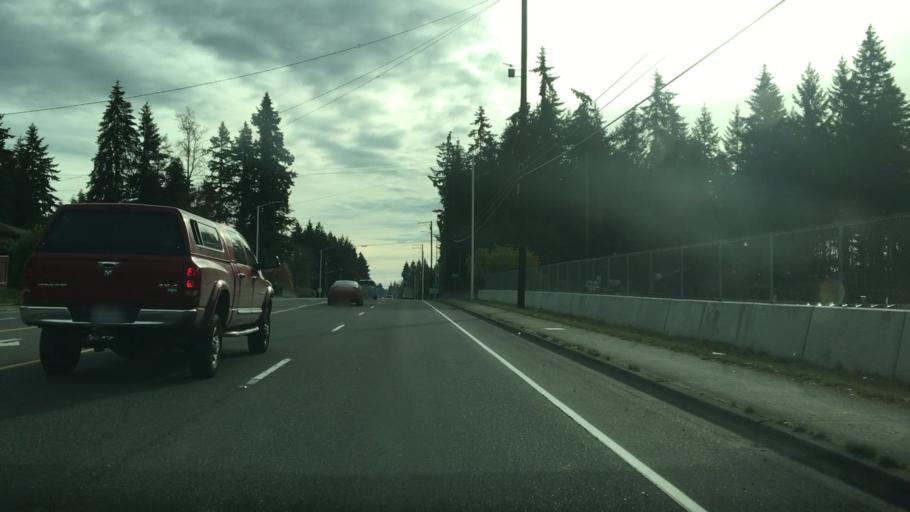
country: US
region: Washington
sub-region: Pierce County
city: South Hill
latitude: 47.1484
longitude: -122.3041
